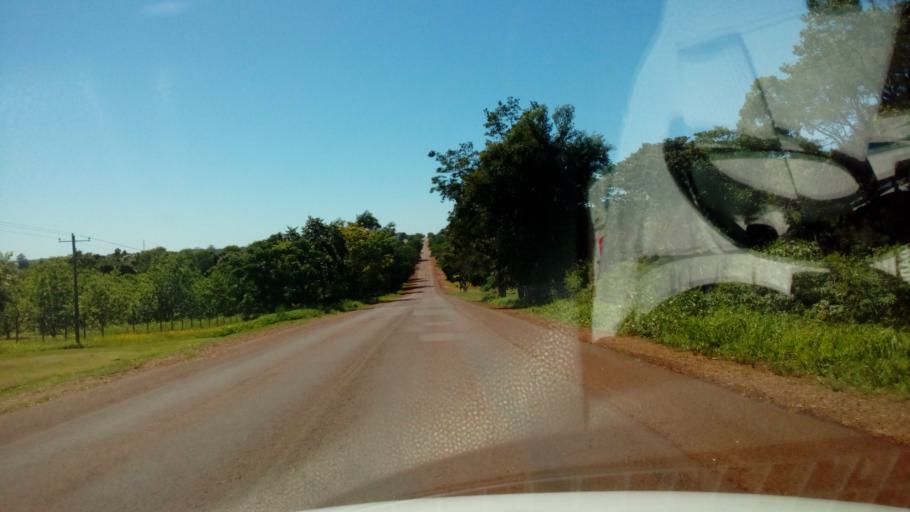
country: AR
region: Misiones
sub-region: Departamento de Leandro N. Alem
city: Leandro N. Alem
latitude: -27.5998
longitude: -55.3468
